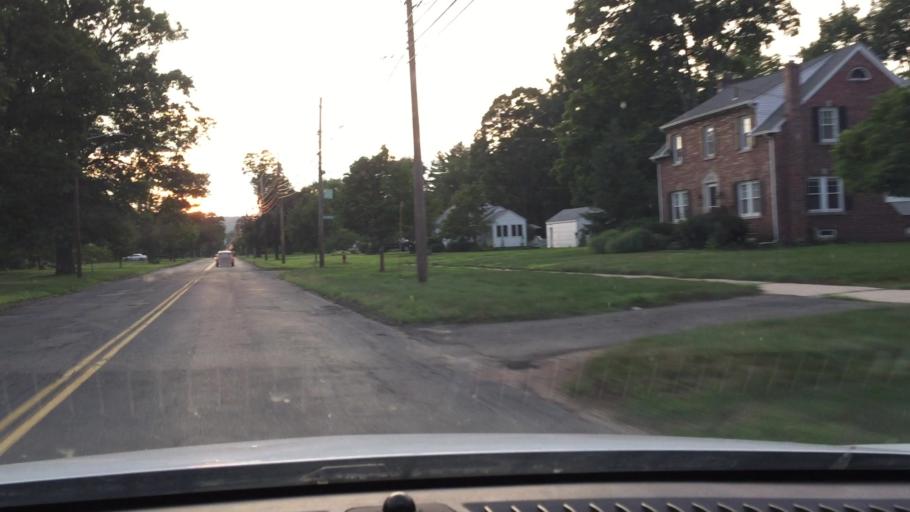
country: US
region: Massachusetts
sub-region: Hampden County
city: Westfield
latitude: 42.1247
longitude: -72.7805
